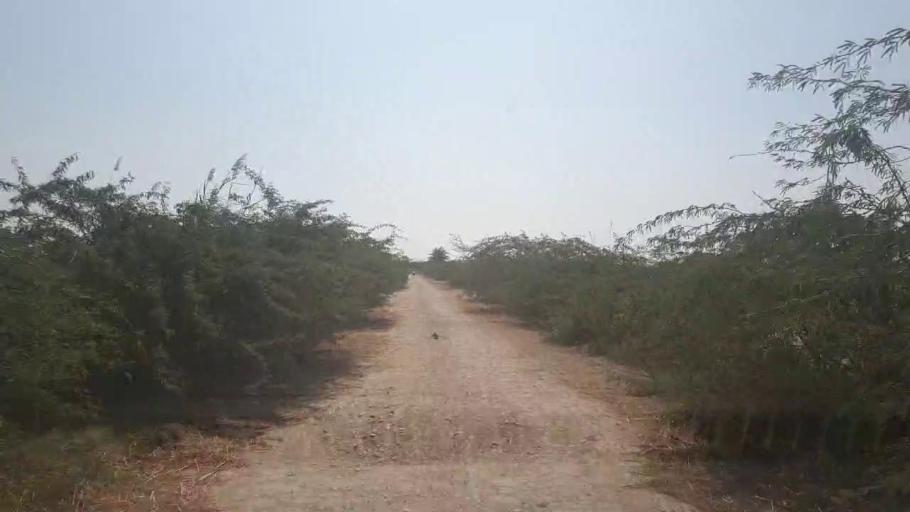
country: PK
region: Sindh
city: Badin
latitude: 24.6486
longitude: 68.9169
